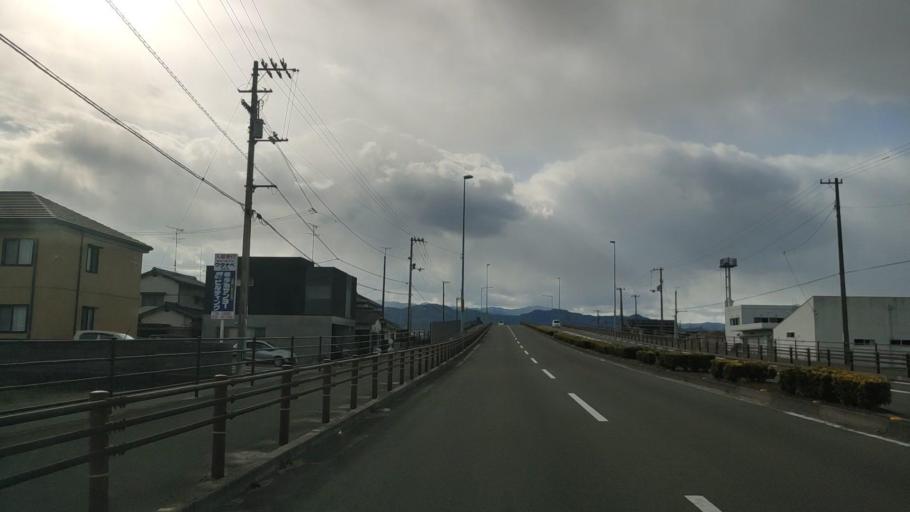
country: JP
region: Ehime
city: Saijo
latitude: 34.0461
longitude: 133.0067
